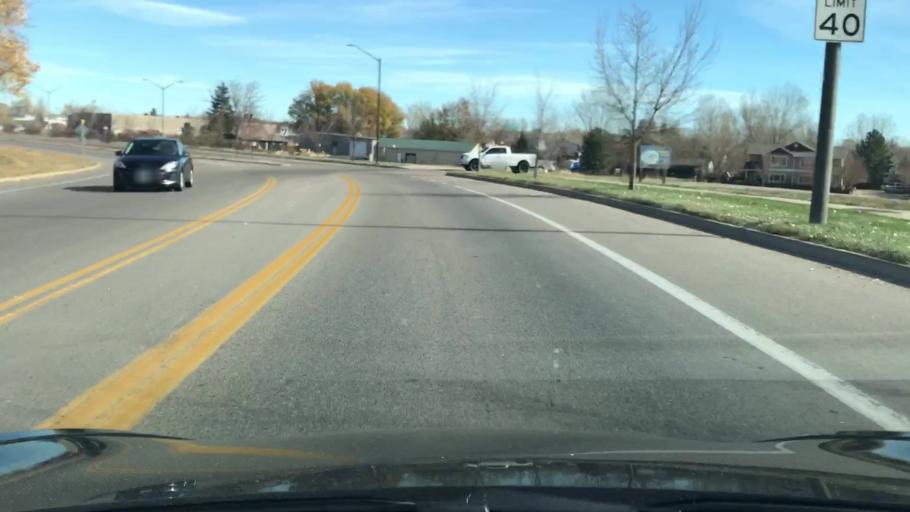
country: US
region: Colorado
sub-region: Larimer County
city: Fort Collins
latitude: 40.5783
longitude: -105.0344
